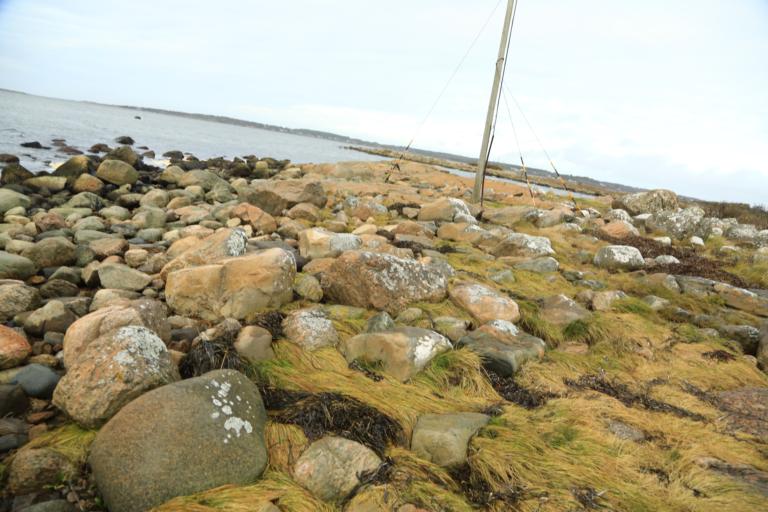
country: SE
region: Halland
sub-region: Varbergs Kommun
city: Varberg
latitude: 57.1727
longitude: 12.2026
